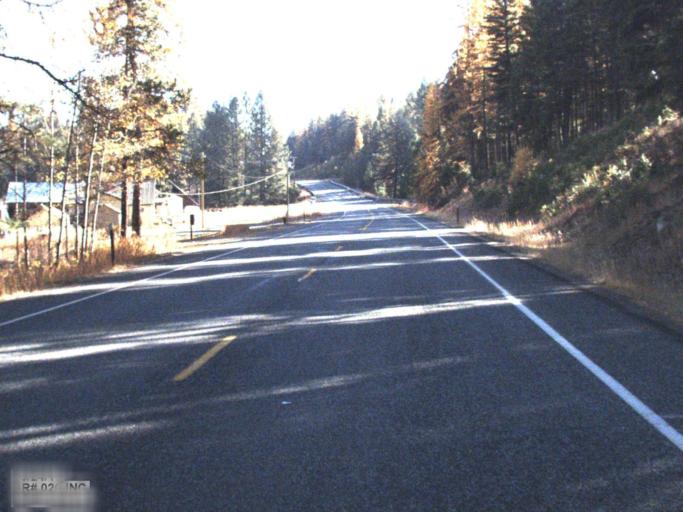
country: US
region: Washington
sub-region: Ferry County
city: Republic
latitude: 48.6580
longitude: -118.8148
